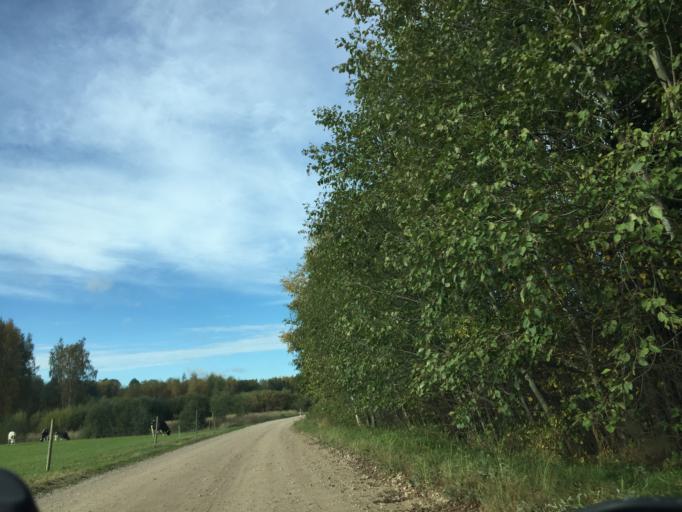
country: LV
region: Jaunpils
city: Jaunpils
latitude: 56.6086
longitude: 23.0520
